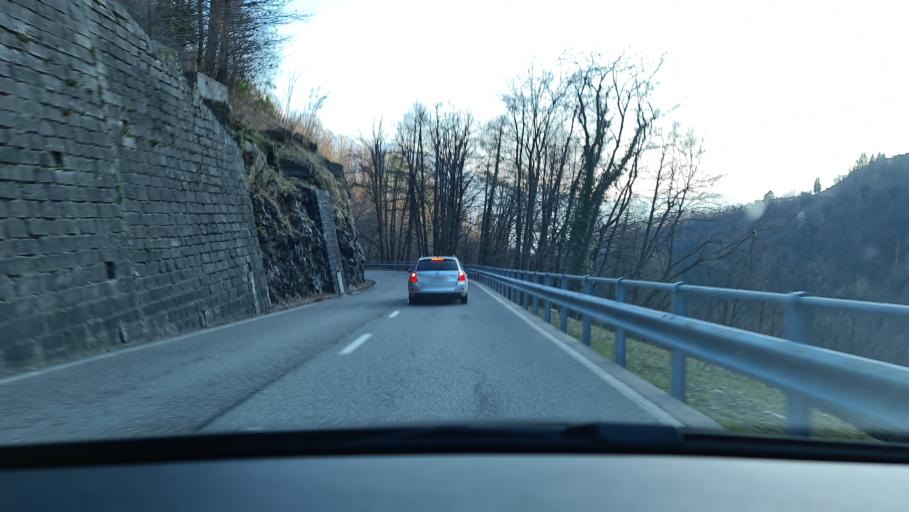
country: CH
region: Ticino
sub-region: Locarno District
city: Gordola
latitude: 46.1944
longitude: 8.8506
